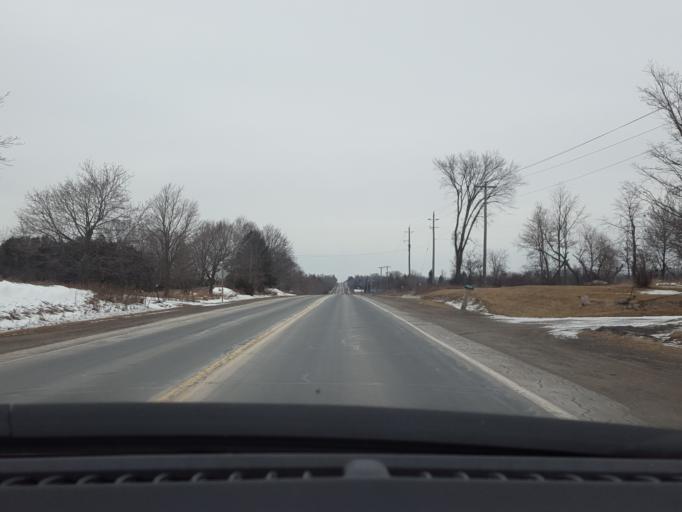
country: CA
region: Ontario
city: Newmarket
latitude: 44.1136
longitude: -79.4182
